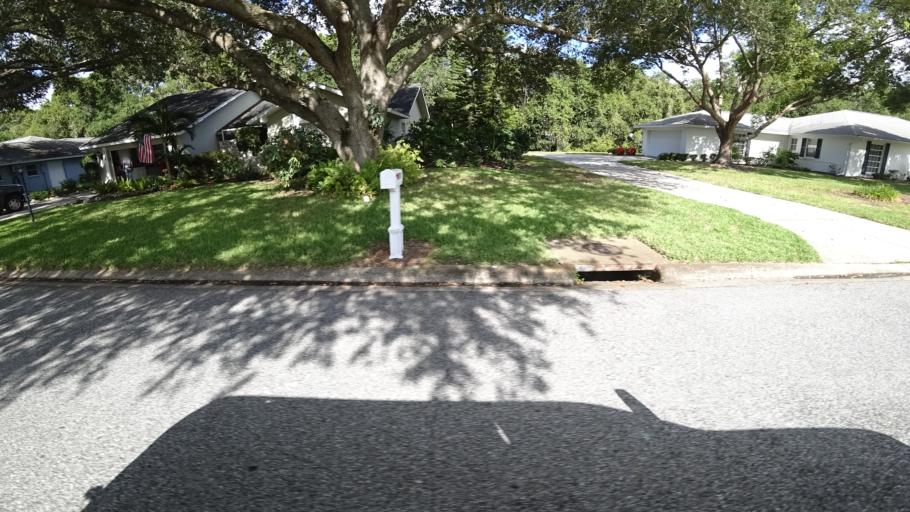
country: US
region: Florida
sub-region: Sarasota County
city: Desoto Lakes
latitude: 27.3957
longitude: -82.4887
